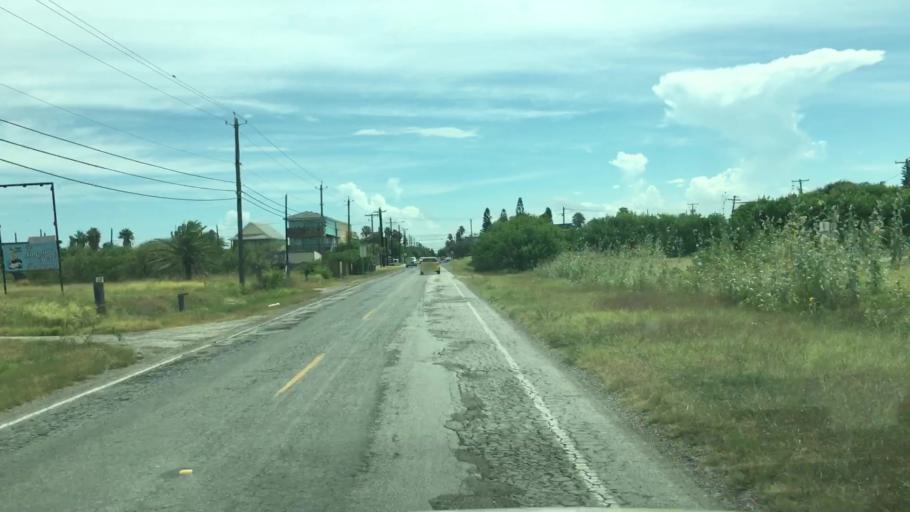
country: US
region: Texas
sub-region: Nueces County
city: Corpus Christi
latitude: 27.6328
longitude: -97.2897
